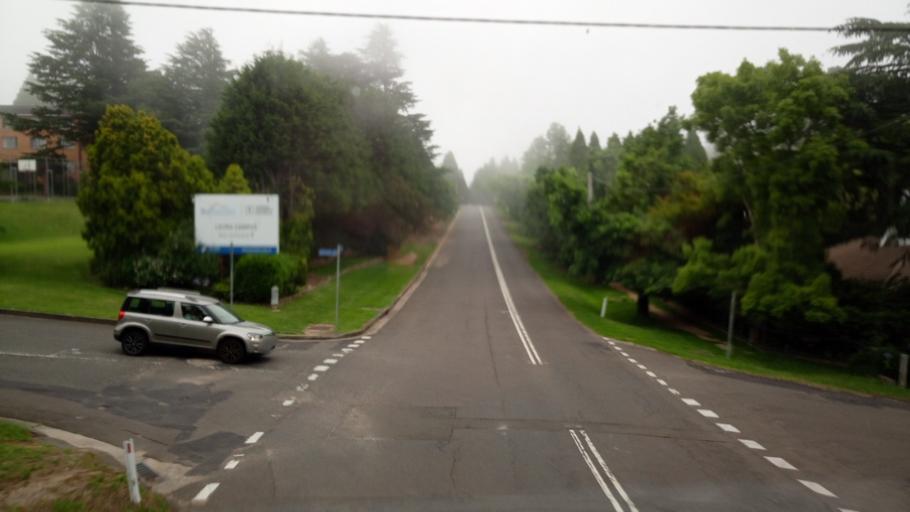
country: AU
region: New South Wales
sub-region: Blue Mountains Municipality
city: Leura
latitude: -33.7186
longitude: 150.3415
